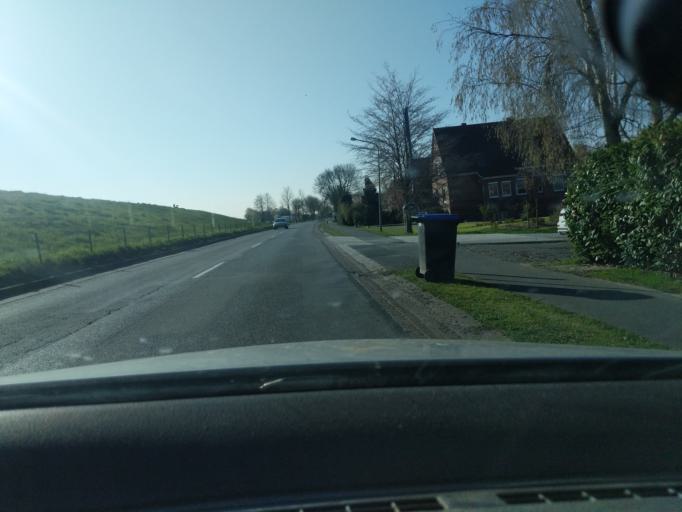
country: DE
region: Lower Saxony
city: Mittelnkirchen
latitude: 53.5636
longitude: 9.6522
